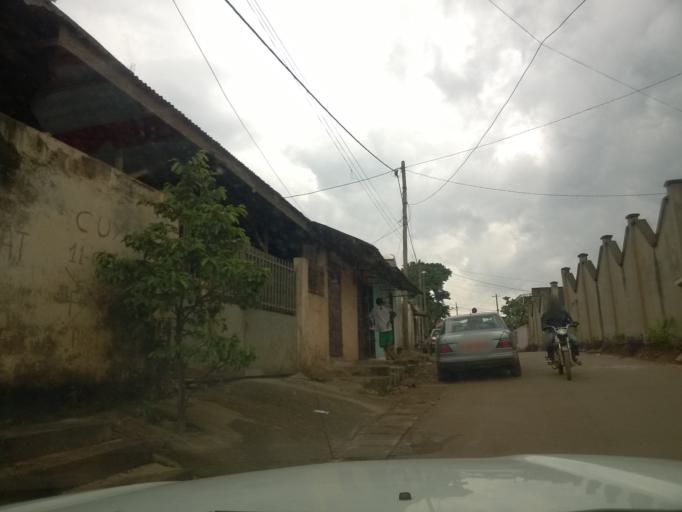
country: CM
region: Centre
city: Yaounde
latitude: 3.9118
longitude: 11.5253
